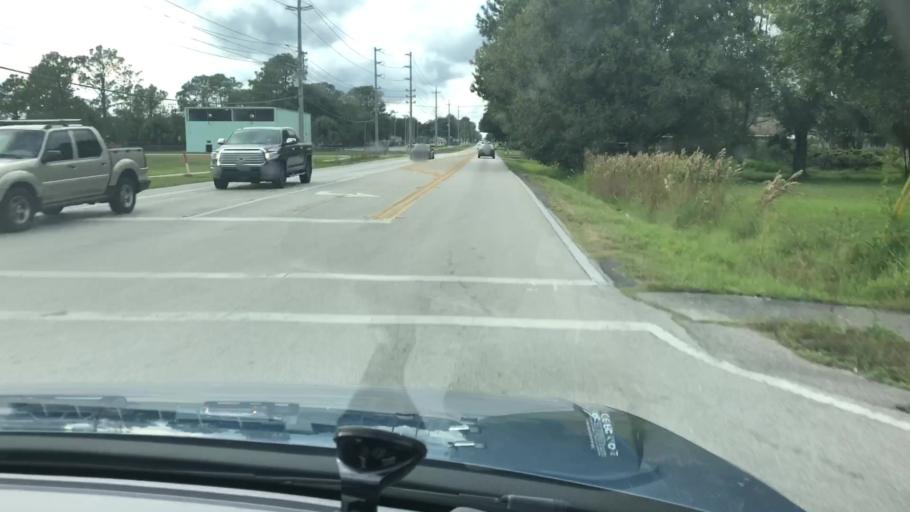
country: US
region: Florida
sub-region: Polk County
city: Gibsonia
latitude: 28.1355
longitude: -81.9862
